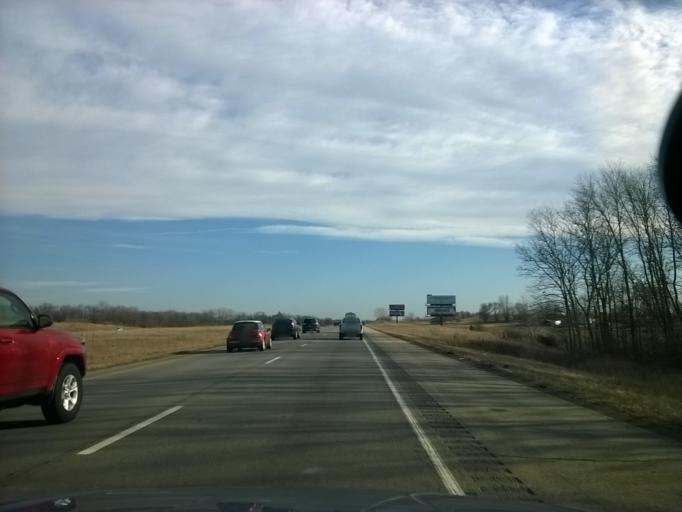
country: US
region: Indiana
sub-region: Johnson County
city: Edinburgh
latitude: 39.4061
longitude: -85.9512
